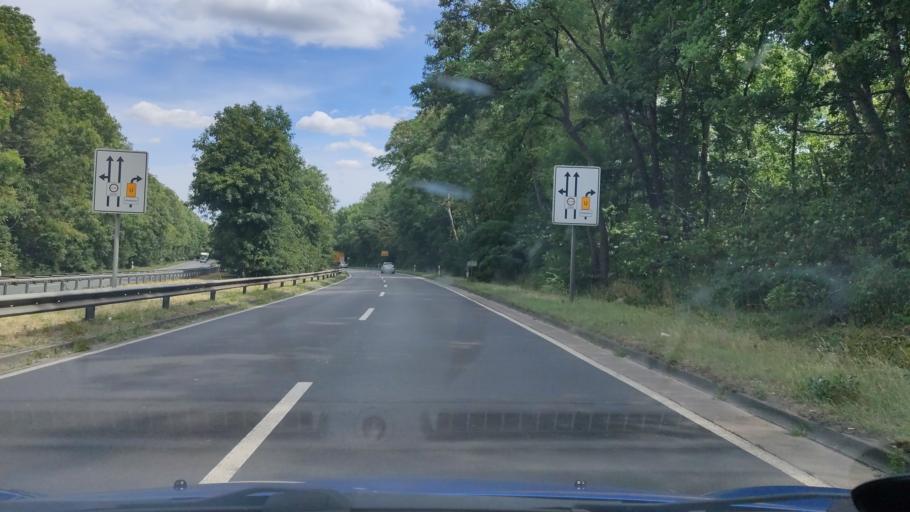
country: DE
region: Lower Saxony
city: Hannover
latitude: 52.3638
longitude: 9.7079
